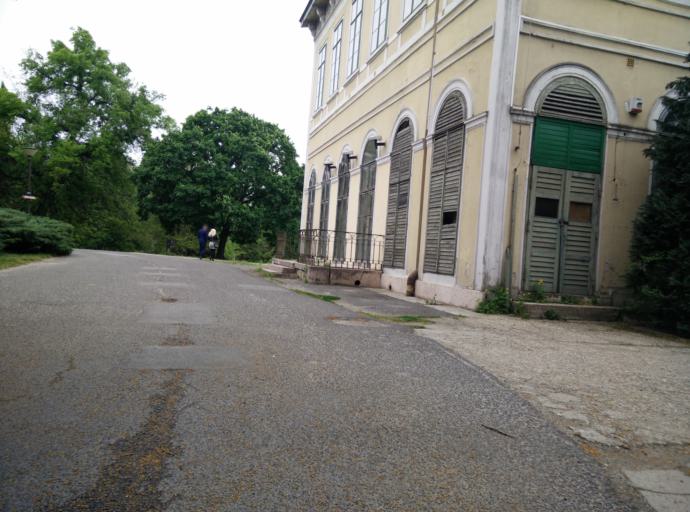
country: HU
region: Pest
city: Fot
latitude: 47.6072
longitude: 19.1956
